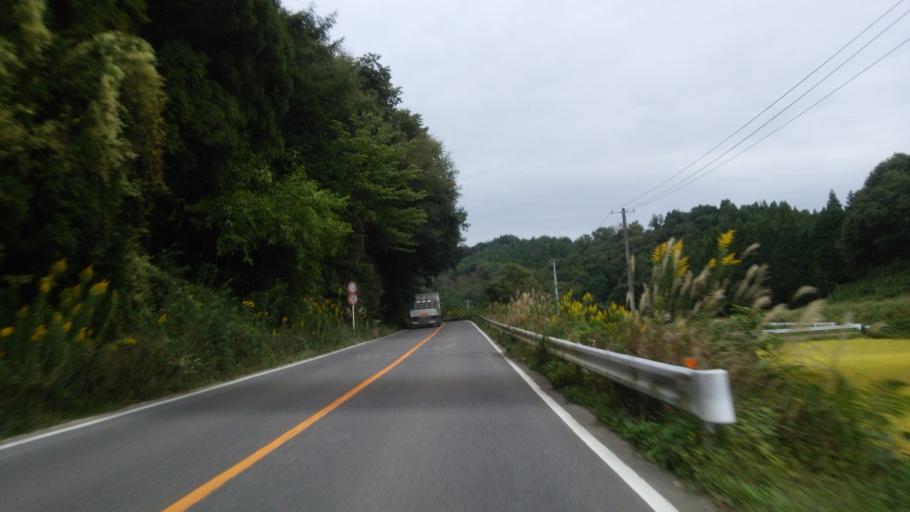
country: JP
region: Fukushima
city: Sukagawa
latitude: 37.2236
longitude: 140.2489
